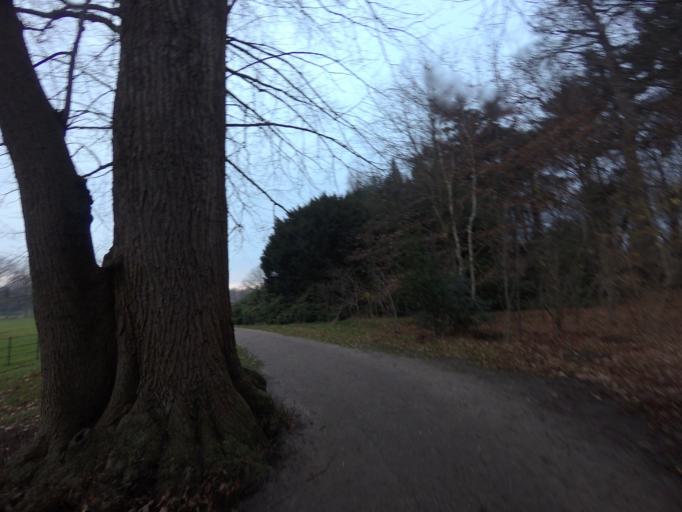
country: NL
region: North Holland
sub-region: Gemeente Wijdemeren
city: Kortenhoef
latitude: 52.2521
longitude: 5.1275
